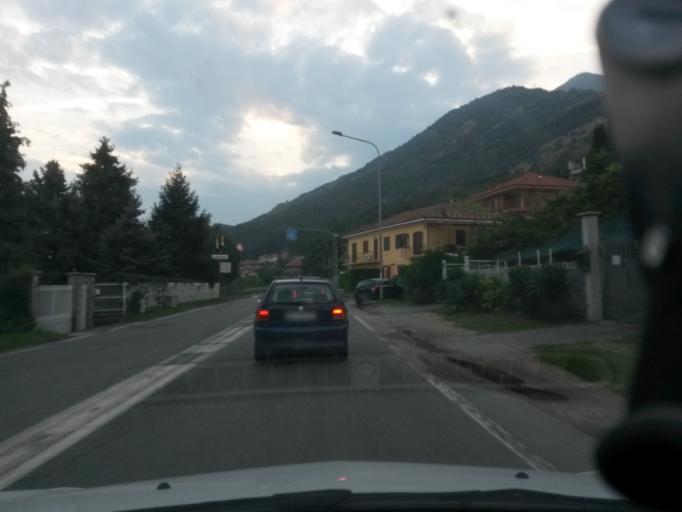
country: IT
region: Piedmont
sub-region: Provincia di Torino
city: Caselette
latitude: 45.1049
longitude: 7.4817
